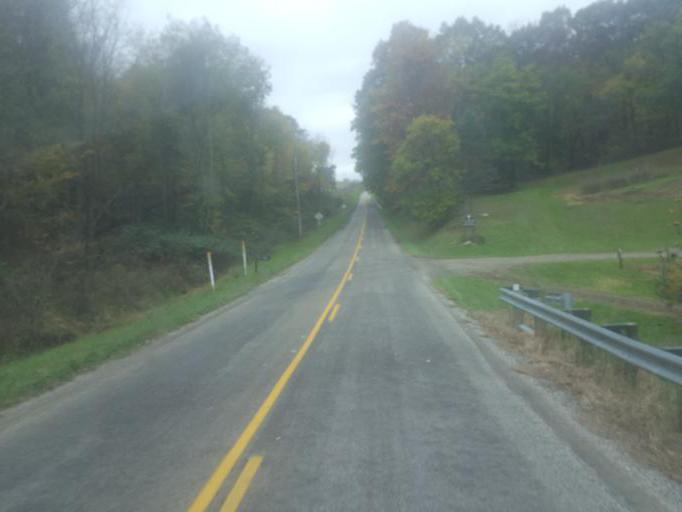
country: US
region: Ohio
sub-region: Ashland County
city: Loudonville
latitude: 40.7321
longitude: -82.3051
